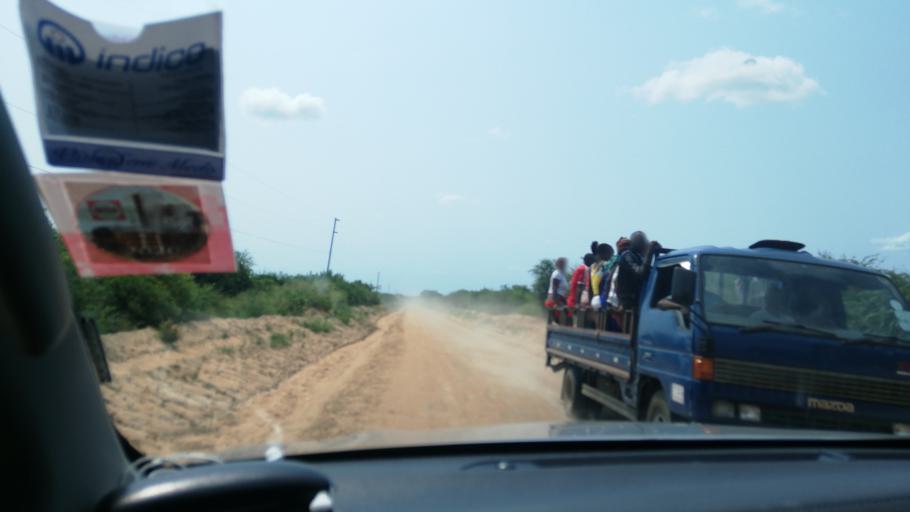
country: MZ
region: Maputo
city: Matola
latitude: -26.0937
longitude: 32.3899
